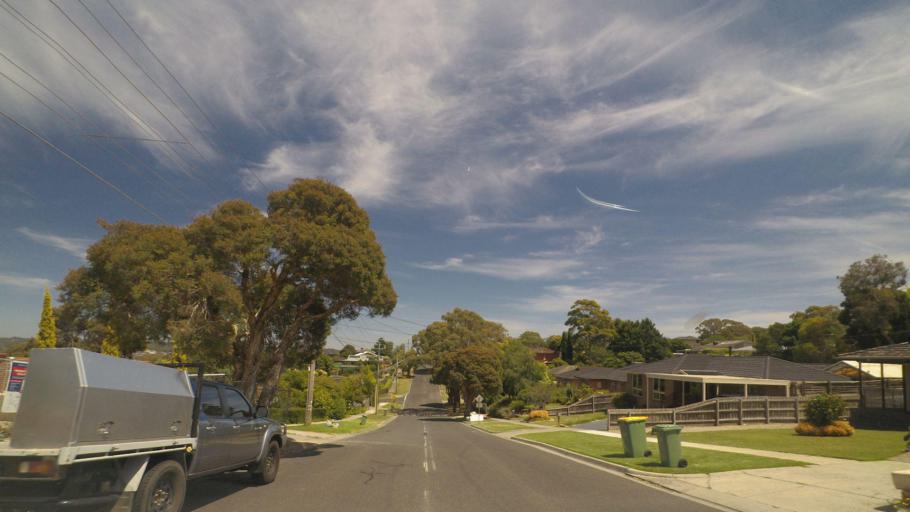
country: AU
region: Victoria
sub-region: Maroondah
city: Croydon North
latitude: -37.7713
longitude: 145.3196
